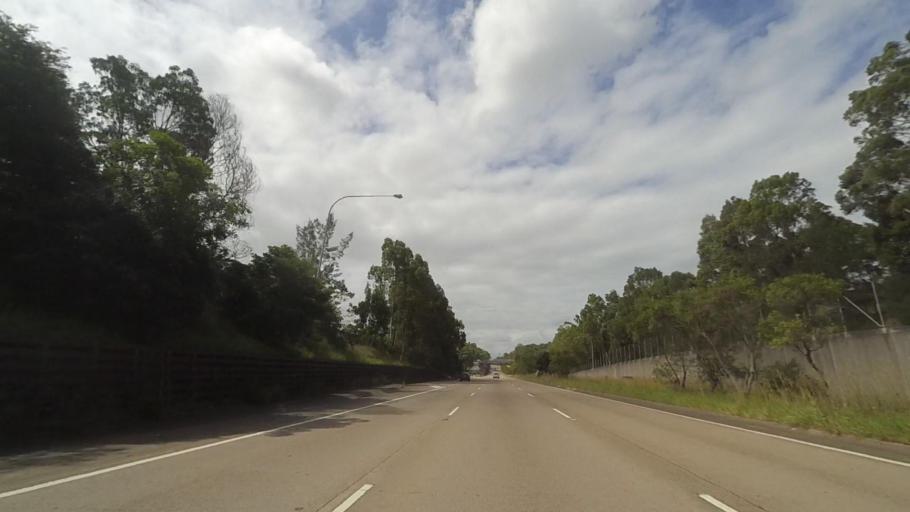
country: AU
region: New South Wales
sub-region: Newcastle
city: North Lambton
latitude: -32.9006
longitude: 151.6939
